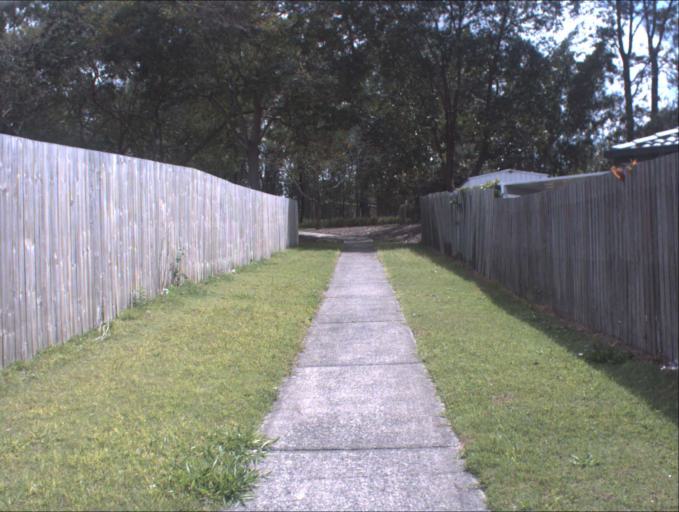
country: AU
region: Queensland
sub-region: Logan
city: Park Ridge South
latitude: -27.6886
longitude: 153.0252
